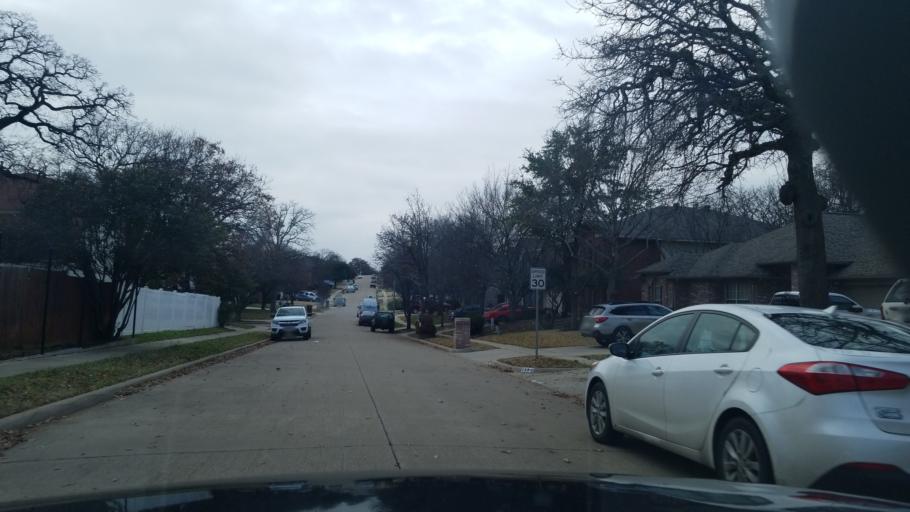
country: US
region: Texas
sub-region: Denton County
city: Corinth
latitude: 33.1421
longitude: -97.0750
